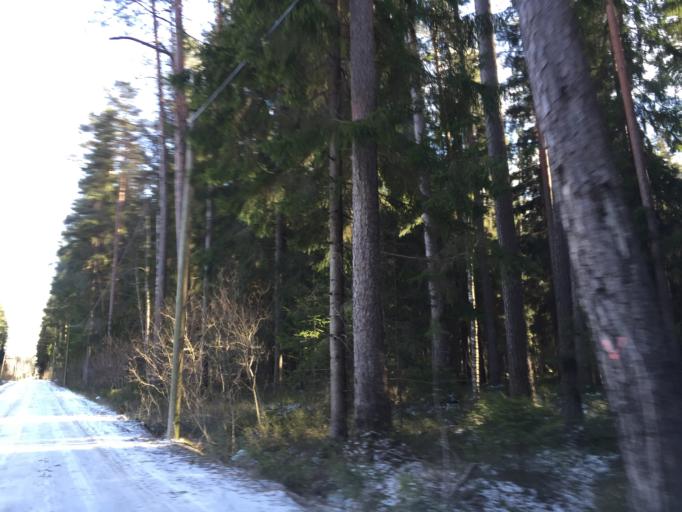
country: LV
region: Garkalne
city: Garkalne
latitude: 56.9519
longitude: 24.4444
